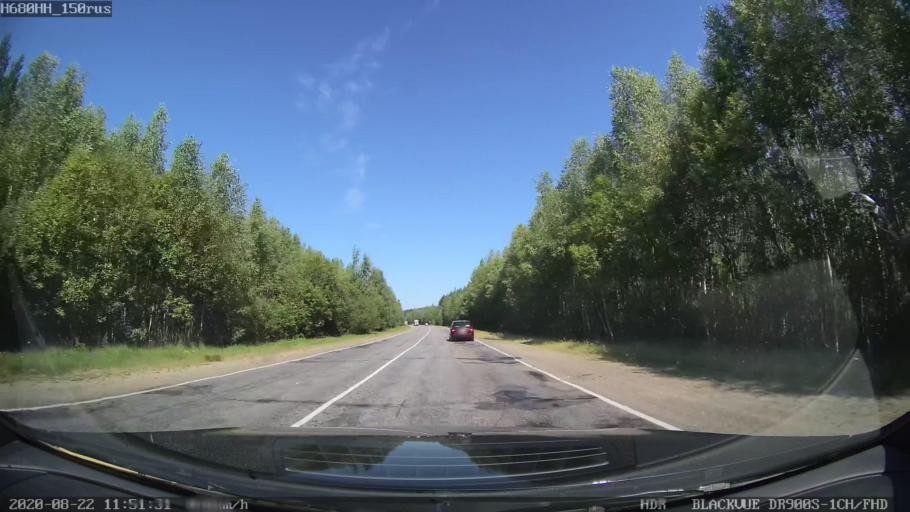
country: RU
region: Tverskaya
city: Sakharovo
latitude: 57.1047
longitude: 36.1205
